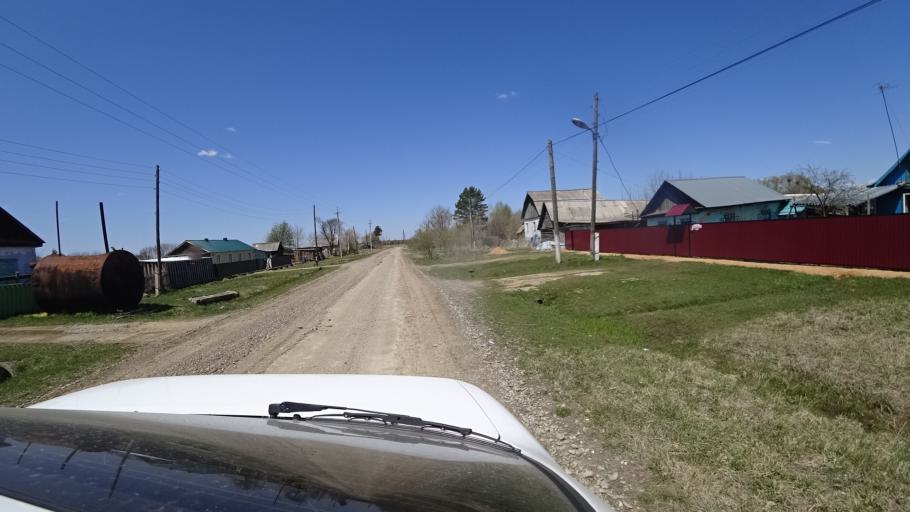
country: RU
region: Primorskiy
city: Lazo
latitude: 45.7998
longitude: 133.7634
